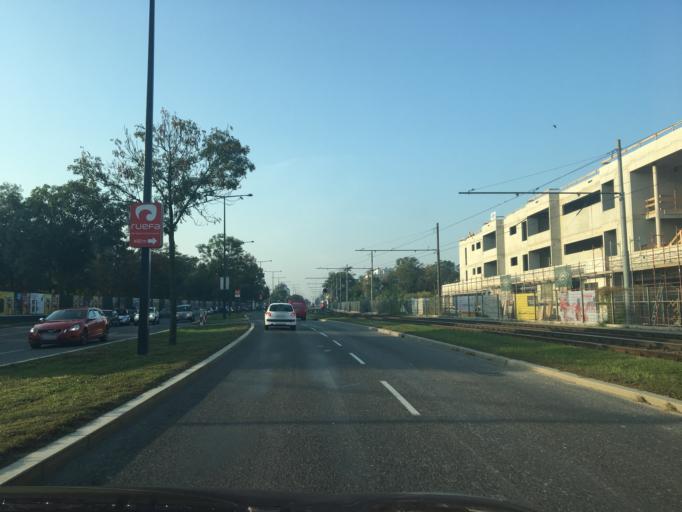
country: AT
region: Lower Austria
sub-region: Politischer Bezirk Korneuburg
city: Hagenbrunn
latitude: 48.2956
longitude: 16.4196
